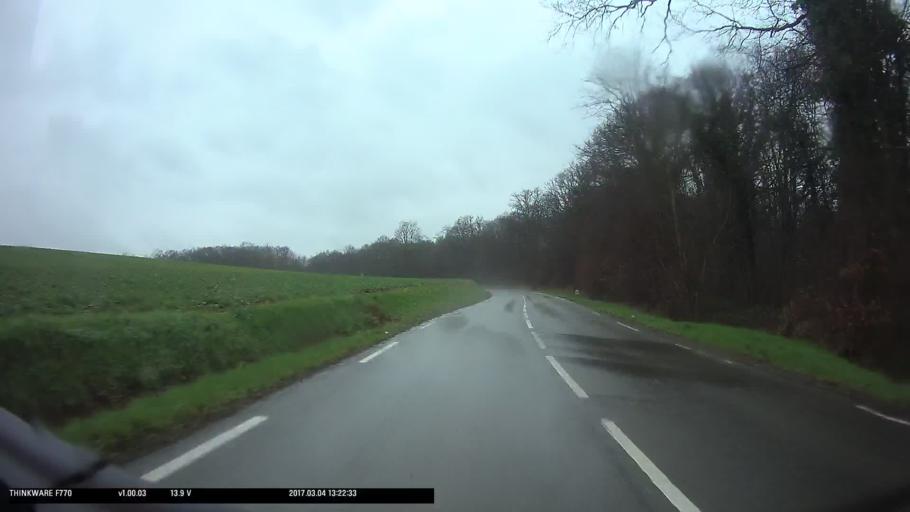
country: FR
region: Ile-de-France
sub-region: Departement du Val-d'Oise
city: Marines
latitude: 49.1260
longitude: 1.9827
